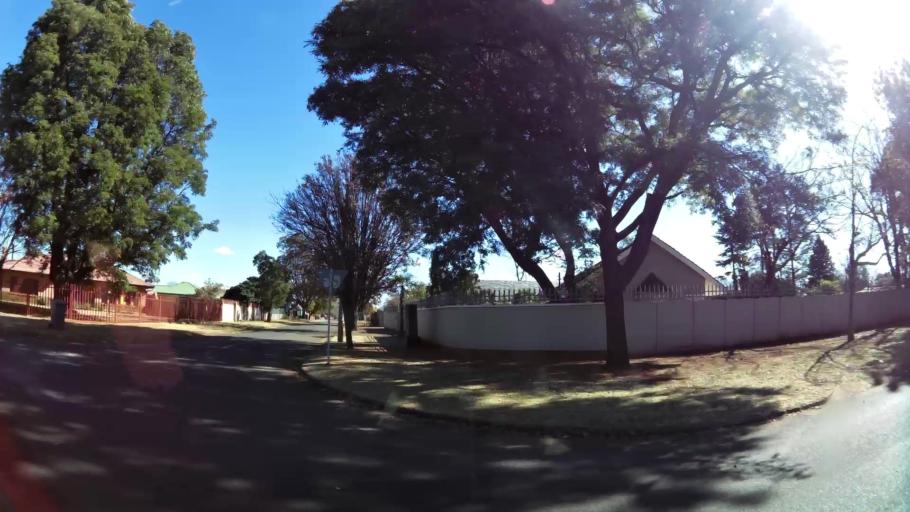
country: ZA
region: Gauteng
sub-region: West Rand District Municipality
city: Carletonville
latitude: -26.3503
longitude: 27.3874
